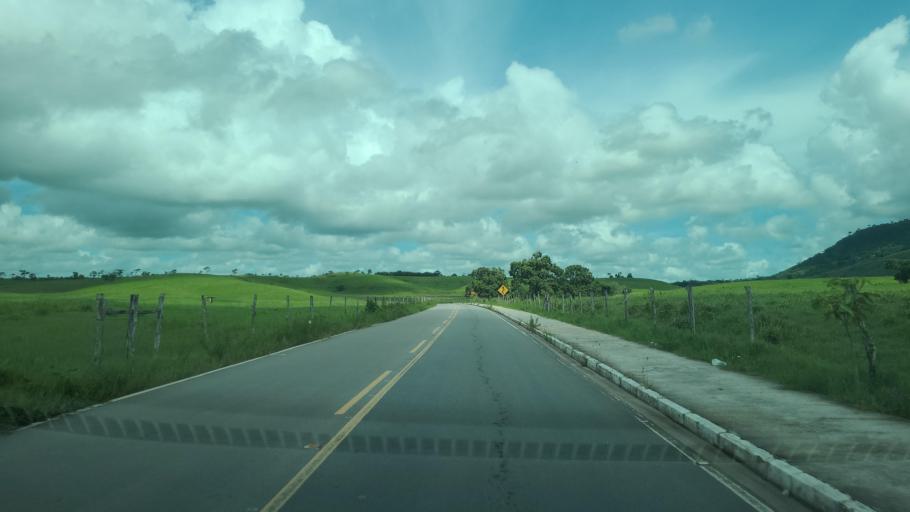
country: BR
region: Alagoas
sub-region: Uniao Dos Palmares
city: Uniao dos Palmares
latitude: -9.1596
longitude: -36.0455
